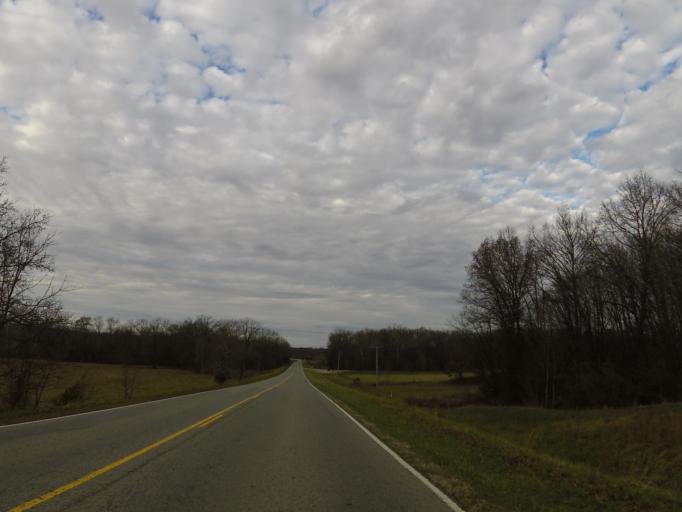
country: US
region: Illinois
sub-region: Jefferson County
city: Mount Vernon
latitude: 38.3771
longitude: -89.0177
